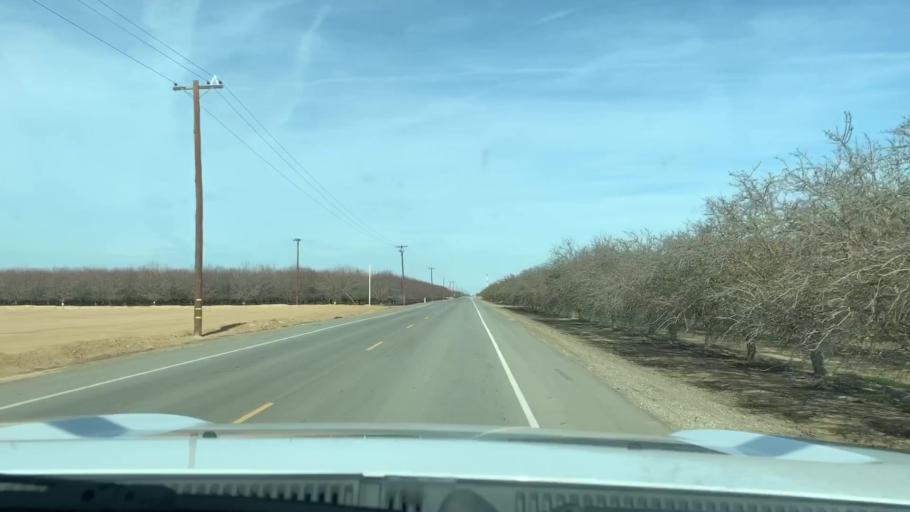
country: US
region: California
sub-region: Kern County
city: Wasco
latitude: 35.5676
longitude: -119.4741
